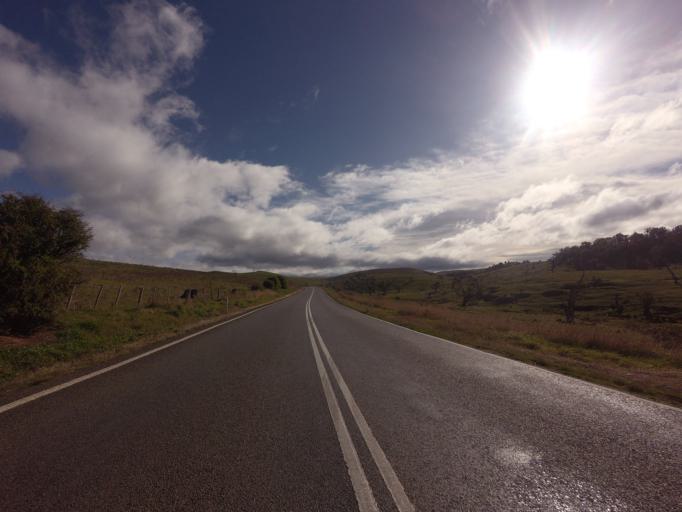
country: AU
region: Tasmania
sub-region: Derwent Valley
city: New Norfolk
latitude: -42.6303
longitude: 146.9122
